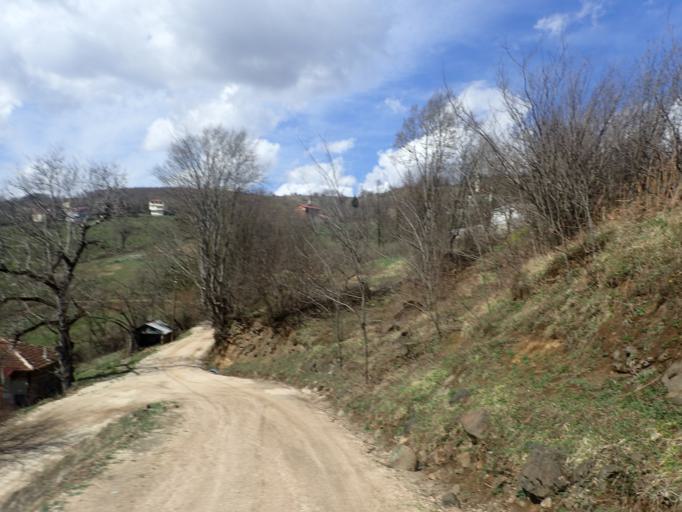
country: TR
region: Ordu
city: Kumru
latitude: 40.8034
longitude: 37.1879
